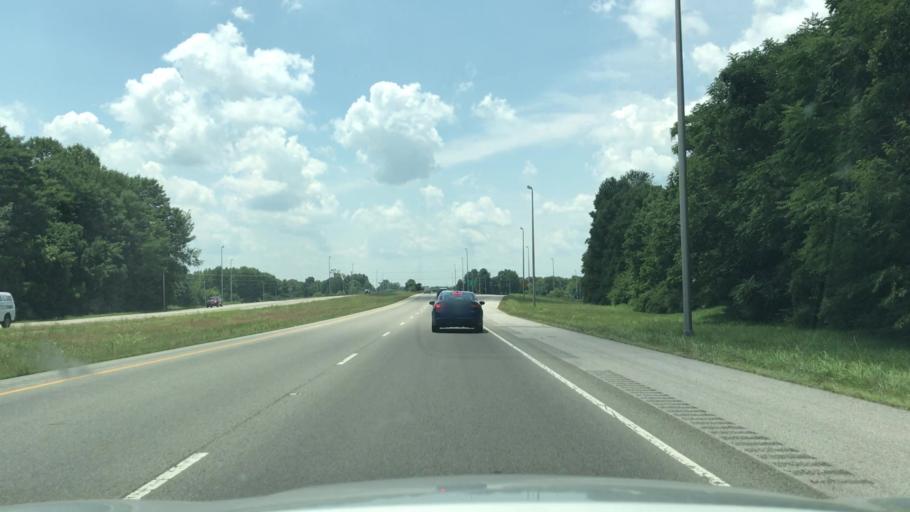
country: US
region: Tennessee
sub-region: Putnam County
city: Cookeville
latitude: 36.1558
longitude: -85.4717
